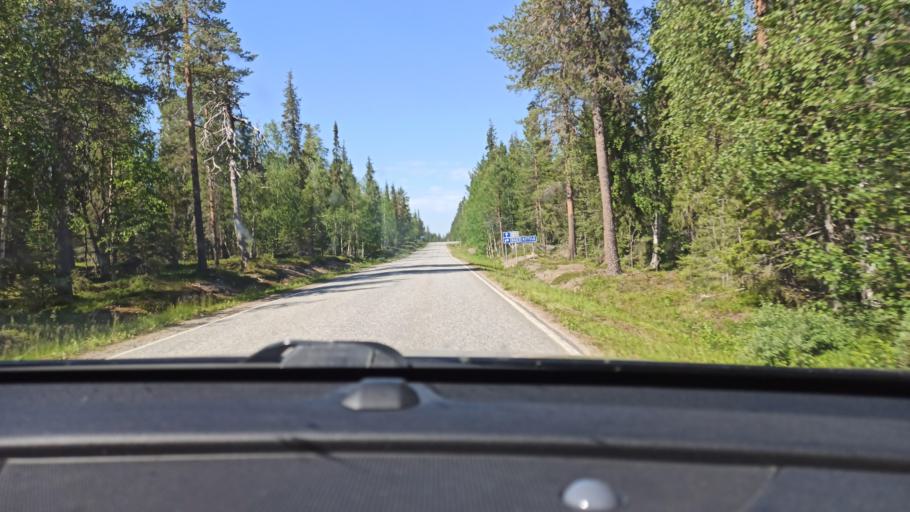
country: FI
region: Lapland
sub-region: Tunturi-Lappi
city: Kolari
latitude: 67.6840
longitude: 24.1173
